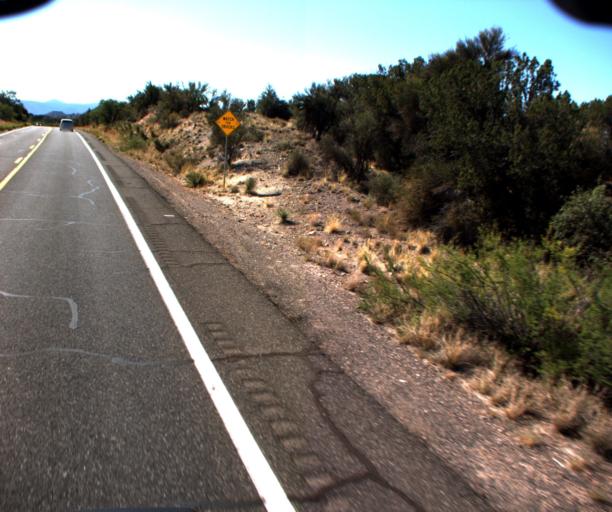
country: US
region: Arizona
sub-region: Yavapai County
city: Lake Montezuma
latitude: 34.7033
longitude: -111.7690
